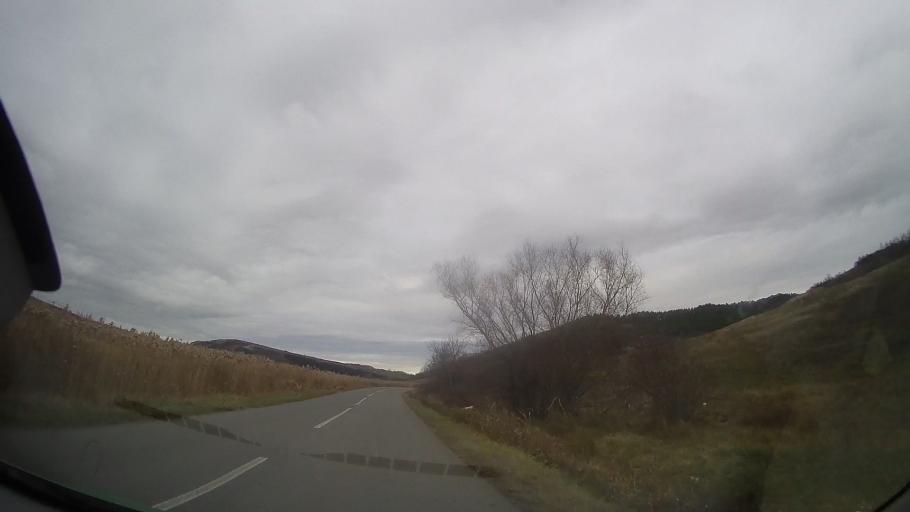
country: RO
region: Mures
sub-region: Comuna Bala
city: Bala
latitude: 46.7201
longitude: 24.5486
